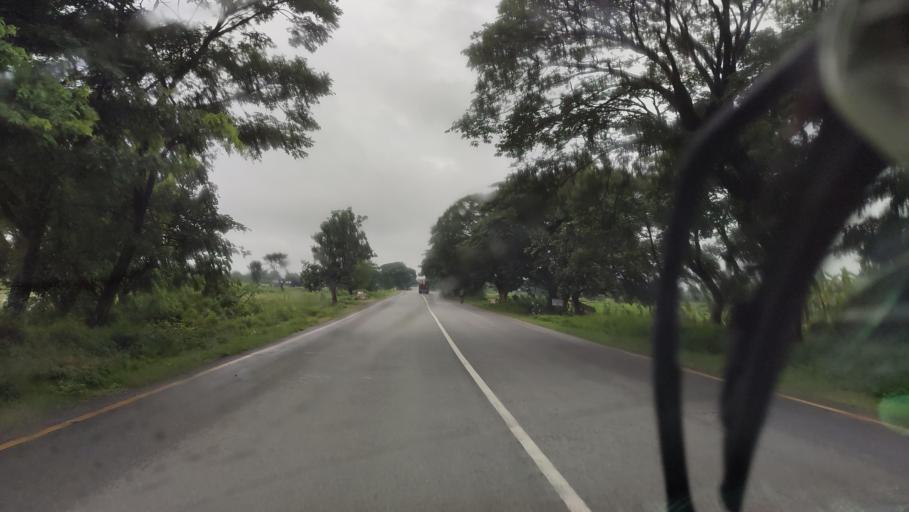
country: MM
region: Mandalay
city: Pyinmana
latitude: 19.9609
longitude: 96.2535
